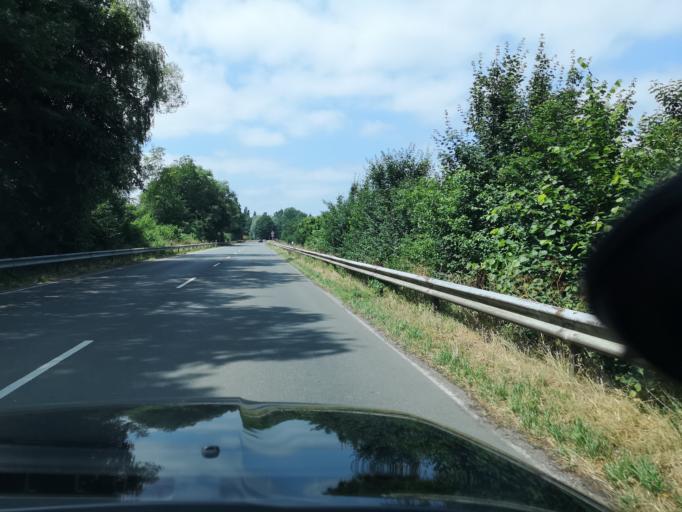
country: DE
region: North Rhine-Westphalia
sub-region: Regierungsbezirk Munster
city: Isselburg
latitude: 51.8551
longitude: 6.4777
